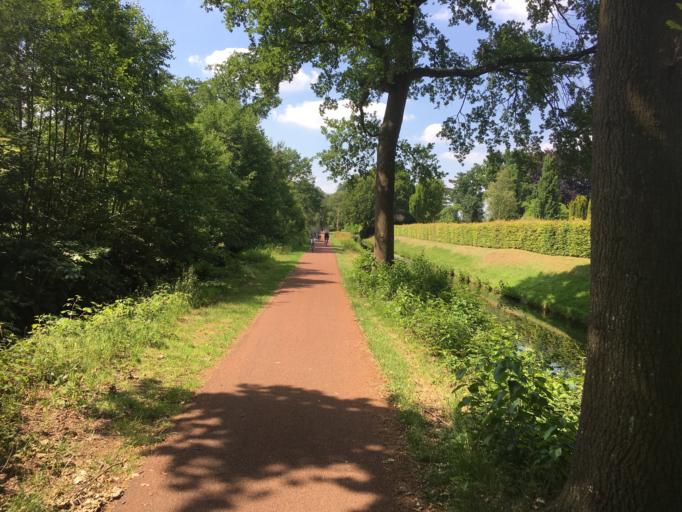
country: NL
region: Friesland
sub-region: Gemeente Heerenveen
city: Oranjewoud
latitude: 52.9497
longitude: 5.9398
